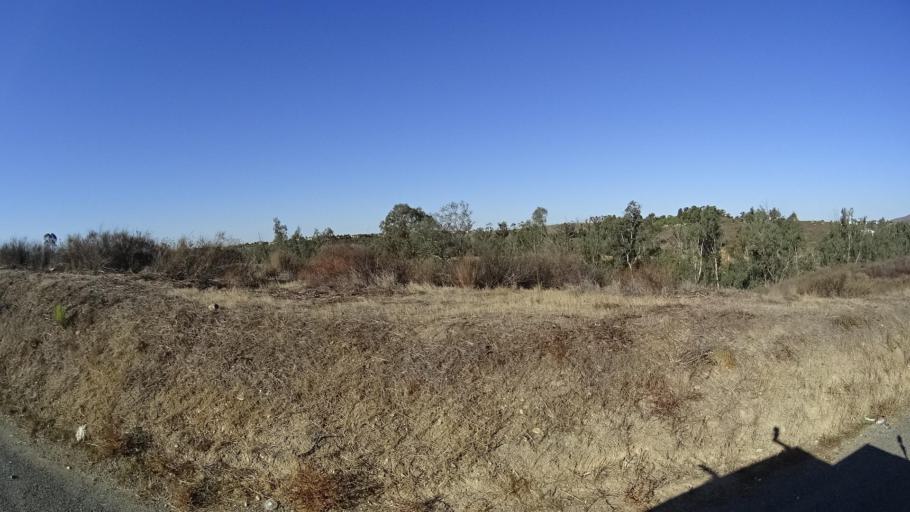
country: US
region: California
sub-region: San Diego County
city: Jamul
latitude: 32.6459
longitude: -116.9273
